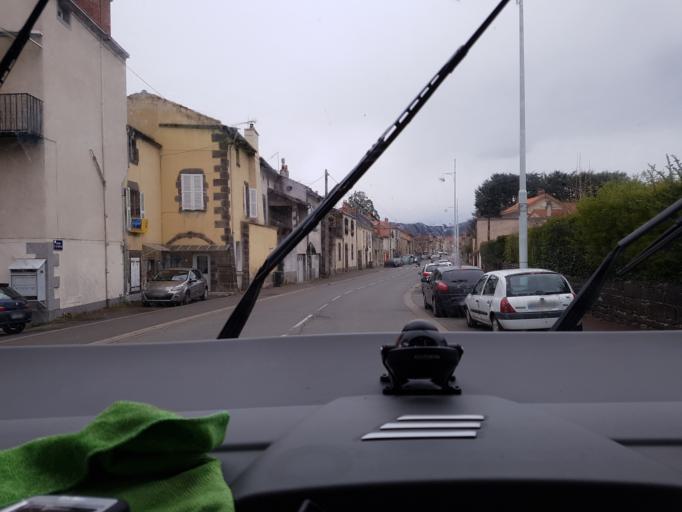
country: FR
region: Auvergne
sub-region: Departement du Puy-de-Dome
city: Mozac
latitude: 45.8932
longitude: 3.1040
